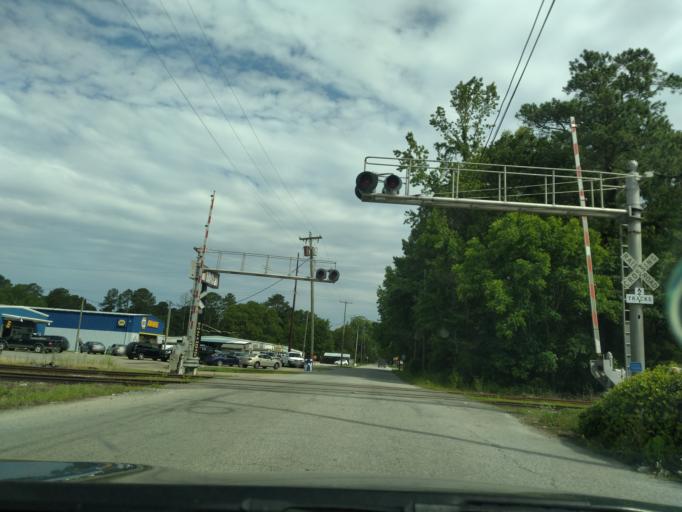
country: US
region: North Carolina
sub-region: Washington County
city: Plymouth
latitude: 35.8576
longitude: -76.7486
